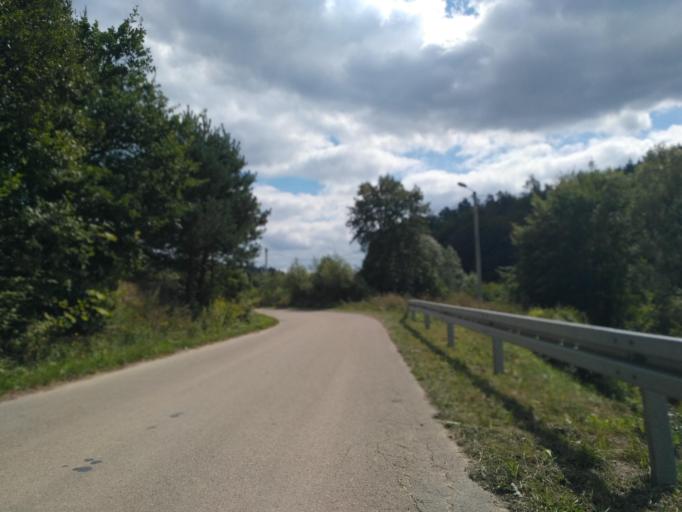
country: PL
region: Subcarpathian Voivodeship
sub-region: Powiat rzeszowski
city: Dynow
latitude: 49.7735
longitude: 22.2531
